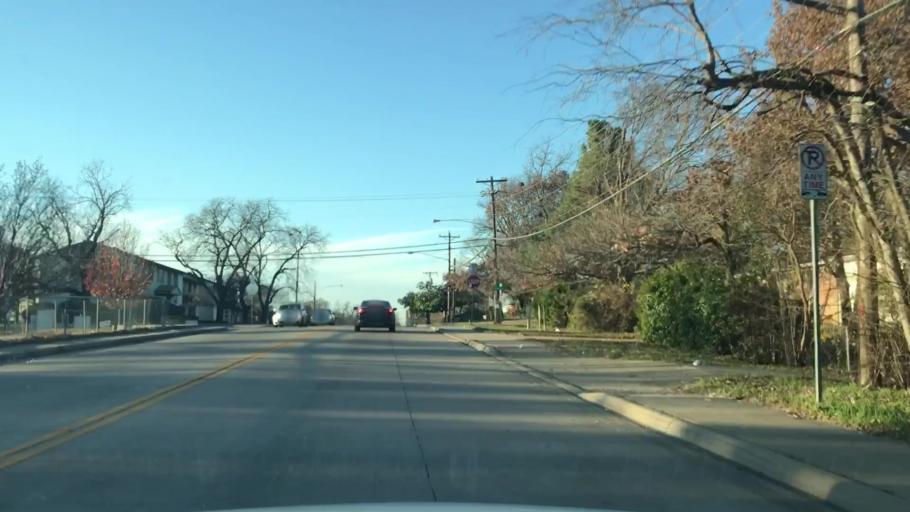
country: US
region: Texas
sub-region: Dallas County
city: Highland Park
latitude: 32.7969
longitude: -96.7083
